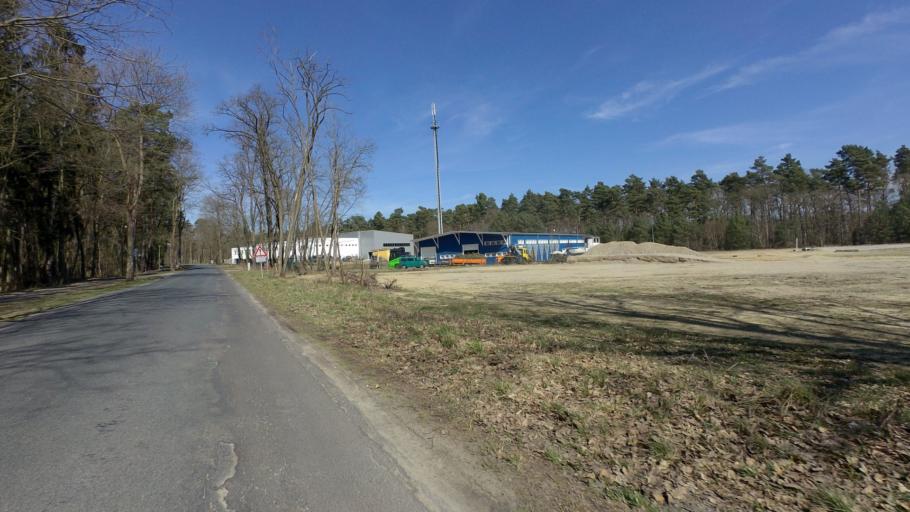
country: DE
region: Brandenburg
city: Bad Saarow
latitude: 52.2791
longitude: 14.0655
